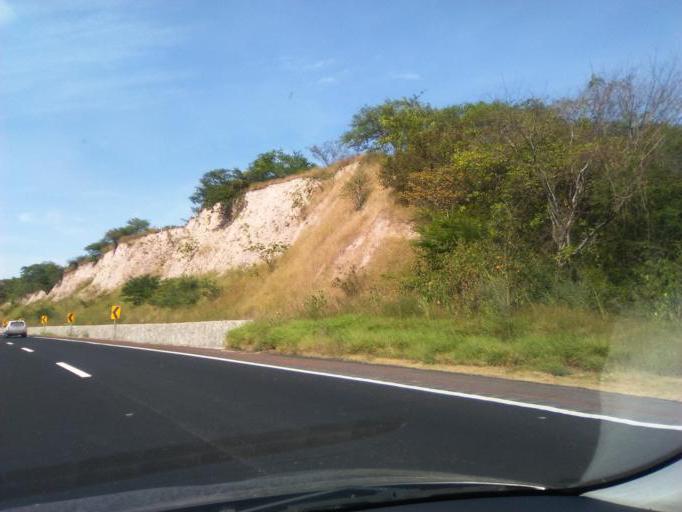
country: MX
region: Morelos
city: Tilzapotla
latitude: 18.4647
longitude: -99.1704
